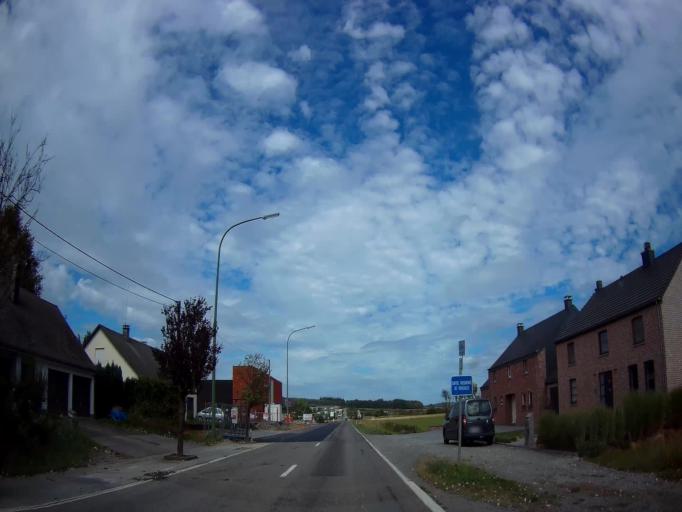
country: BE
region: Wallonia
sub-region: Province du Luxembourg
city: Hotton
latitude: 50.2749
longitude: 5.4523
